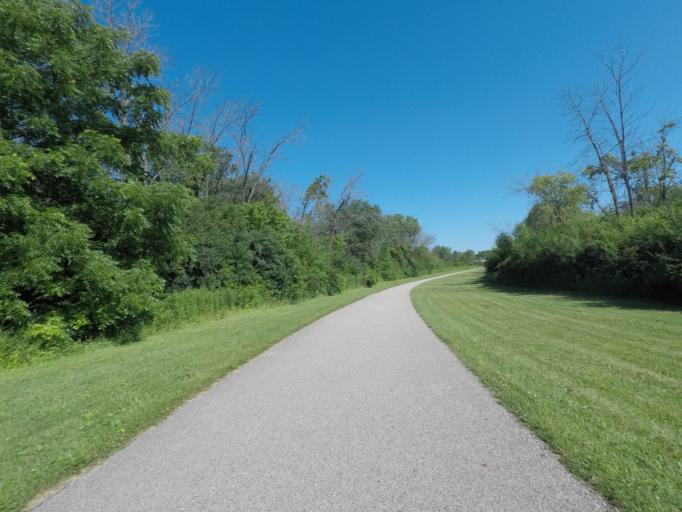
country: US
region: Wisconsin
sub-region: Waukesha County
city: Elm Grove
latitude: 43.0262
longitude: -88.0656
